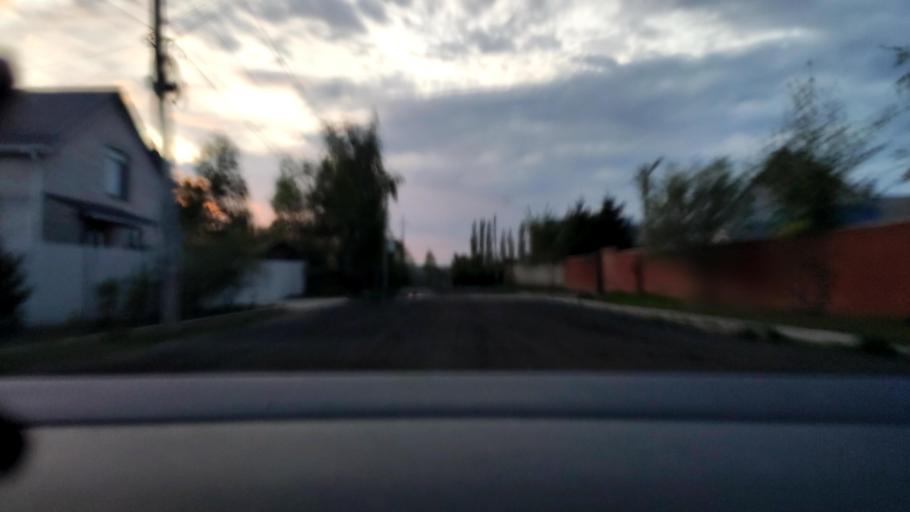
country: RU
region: Voronezj
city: Podgornoye
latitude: 51.7370
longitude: 39.1657
